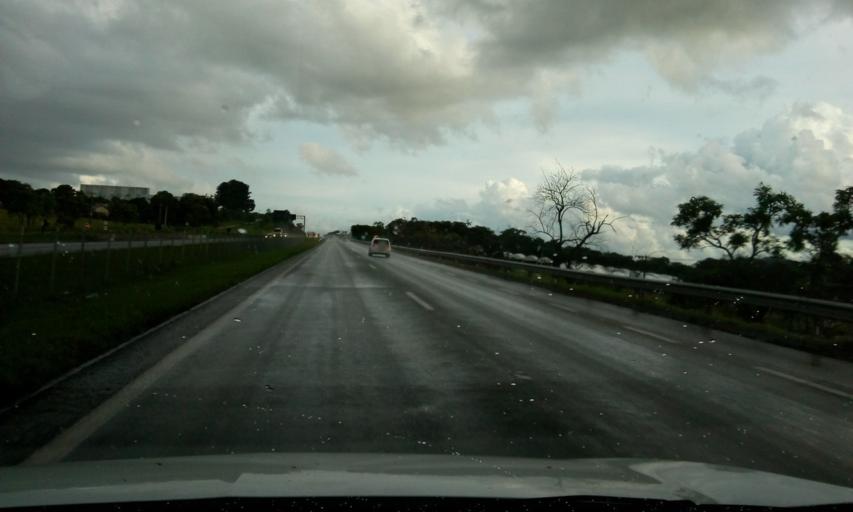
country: BR
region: Sao Paulo
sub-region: Jarinu
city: Jarinu
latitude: -23.0564
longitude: -46.6590
